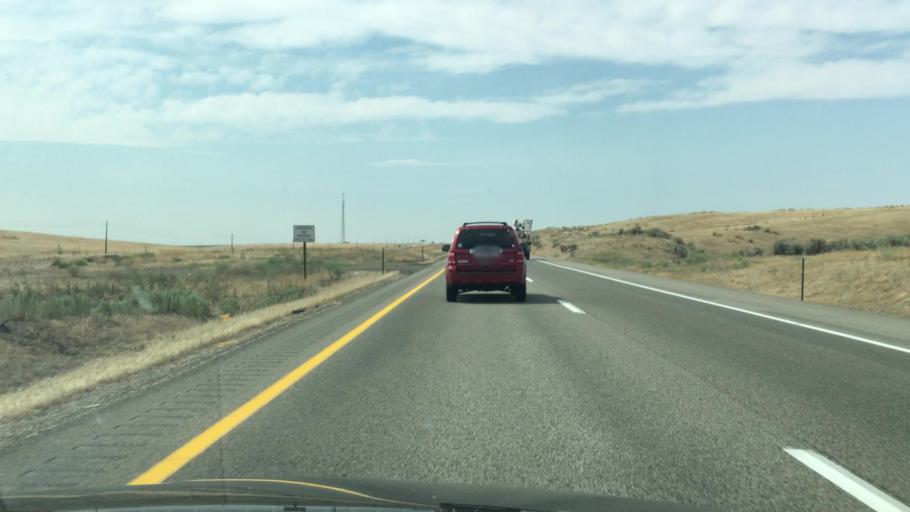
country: US
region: Idaho
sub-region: Ada County
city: Boise
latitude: 43.4424
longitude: -116.0693
